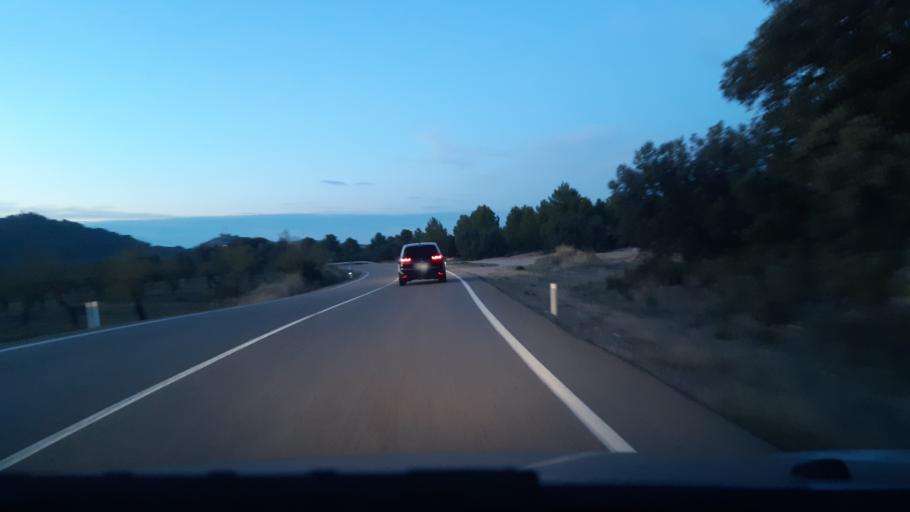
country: ES
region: Aragon
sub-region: Provincia de Teruel
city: Calaceite
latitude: 40.9977
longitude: 0.1959
